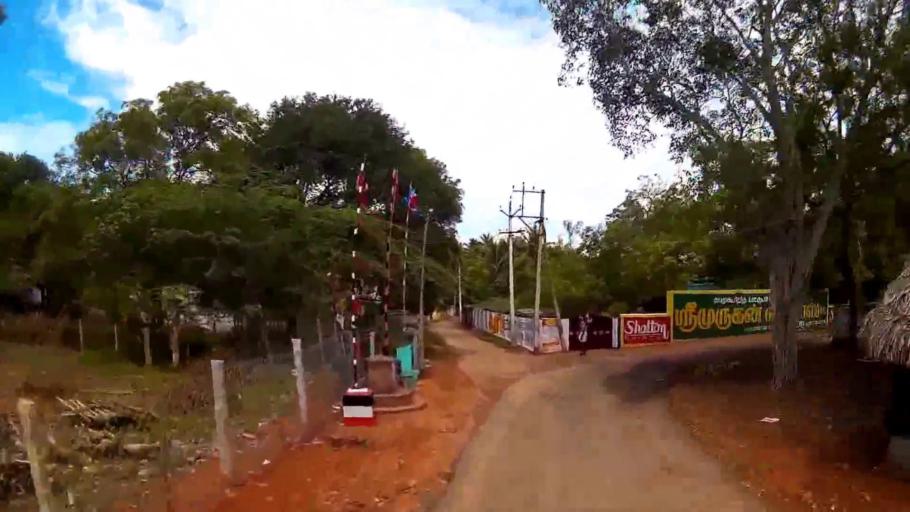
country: VN
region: Lao Cai
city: Sa Pa
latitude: 22.3339
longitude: 103.8417
